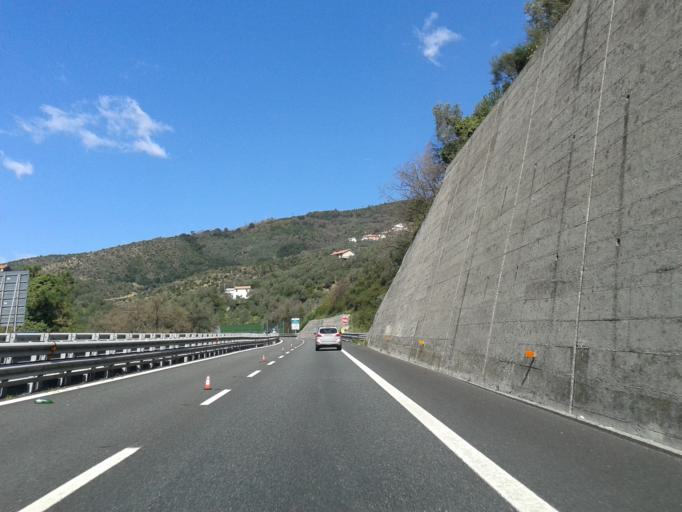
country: IT
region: Liguria
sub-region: Provincia di Genova
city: Sestri Levante
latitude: 44.2820
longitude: 9.4103
